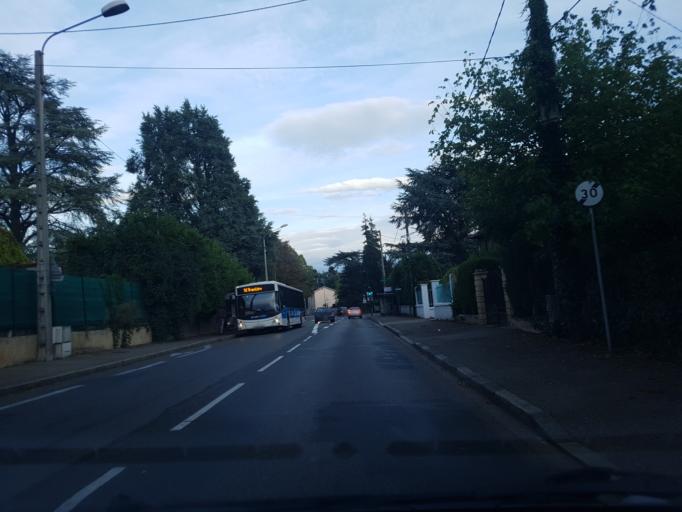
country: FR
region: Rhone-Alpes
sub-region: Departement du Rhone
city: Ecully
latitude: 45.7644
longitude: 4.7590
